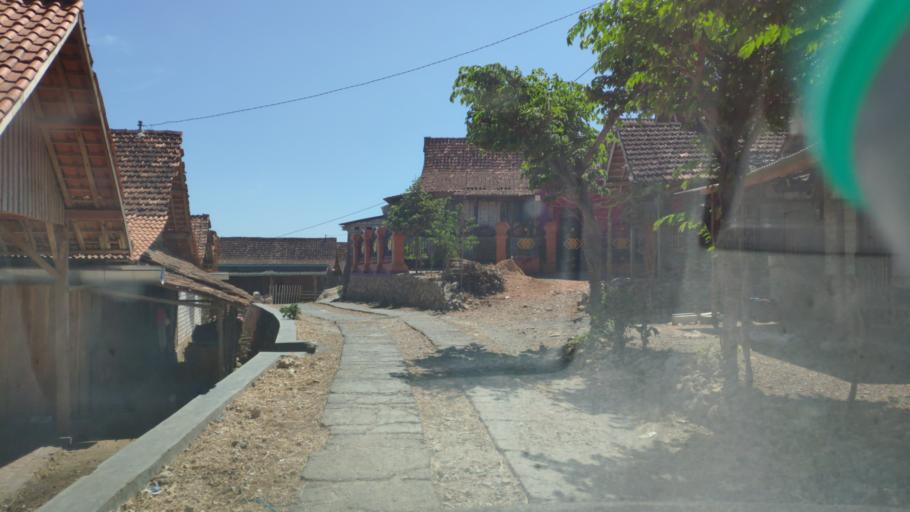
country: ID
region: Central Java
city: Jurangjero
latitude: -6.8958
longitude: 111.5083
